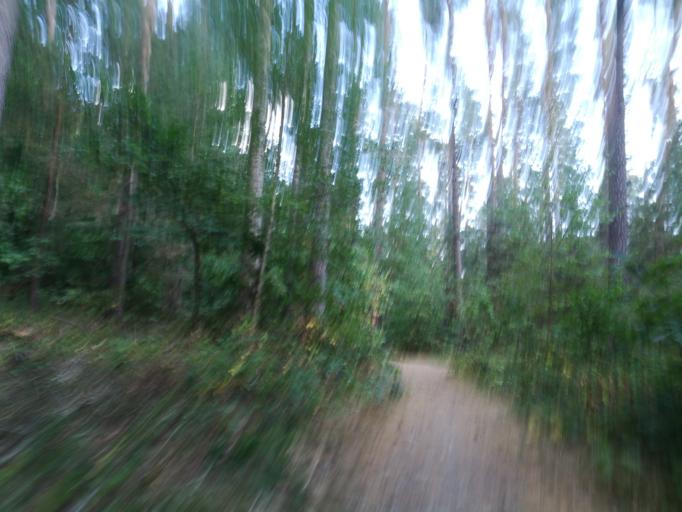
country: DE
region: Bavaria
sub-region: Regierungsbezirk Mittelfranken
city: Seukendorf
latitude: 49.4732
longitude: 10.9146
